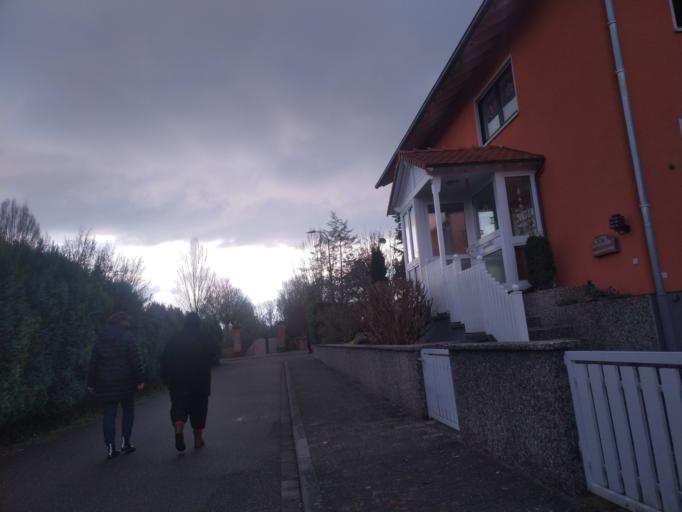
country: DE
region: Rheinland-Pfalz
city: Worth am Rhein
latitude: 49.0286
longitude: 8.2874
